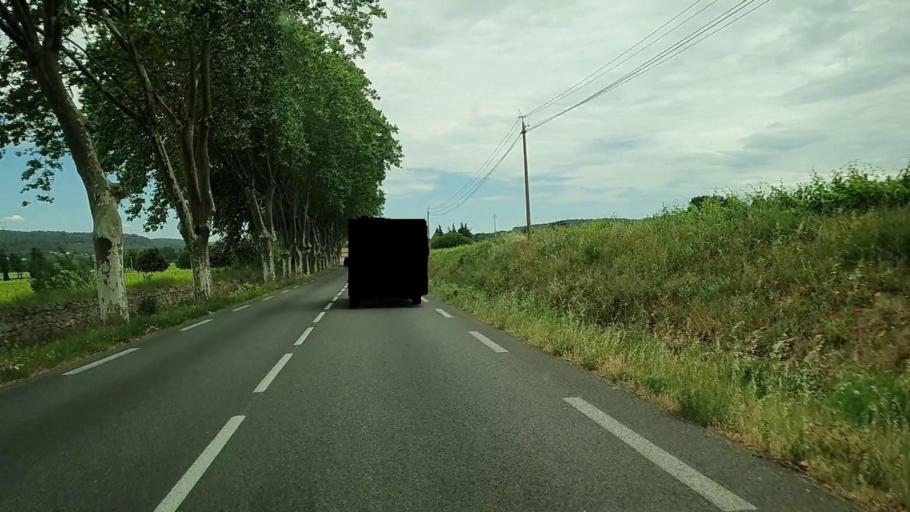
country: FR
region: Languedoc-Roussillon
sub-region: Departement du Gard
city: Tresques
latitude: 44.1188
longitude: 4.6153
